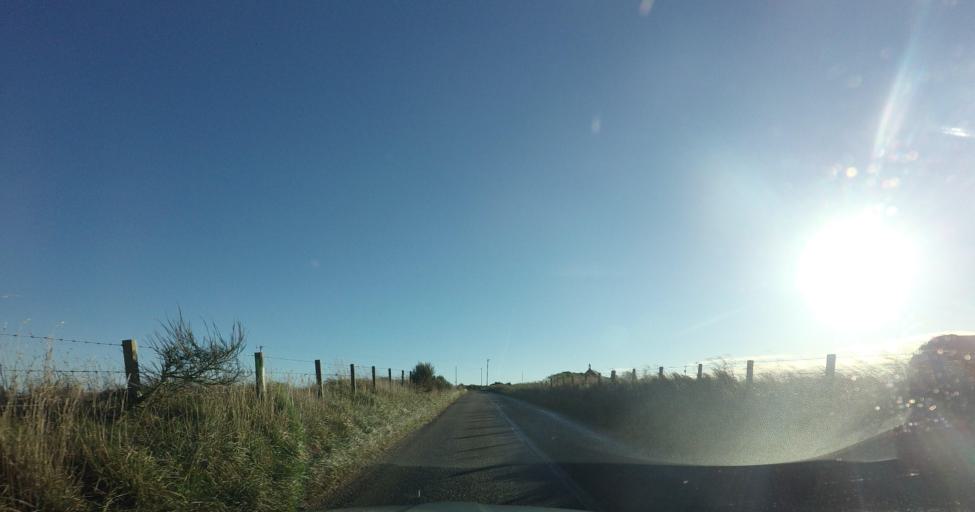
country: GB
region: Scotland
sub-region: Aberdeenshire
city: Macduff
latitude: 57.6586
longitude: -2.3296
